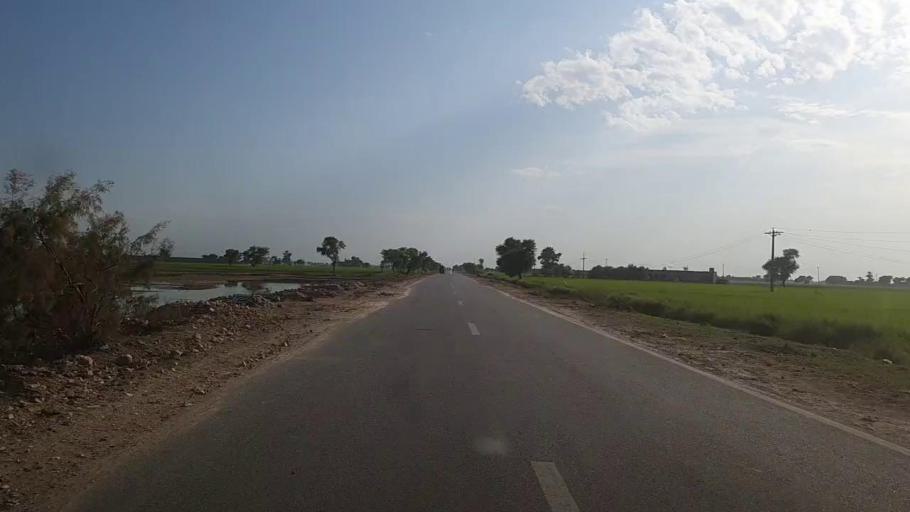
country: PK
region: Sindh
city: Thul
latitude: 28.2158
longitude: 68.7539
